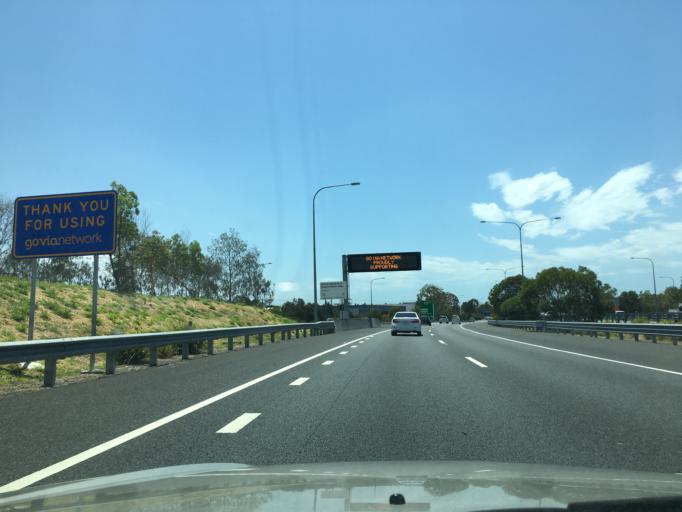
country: AU
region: Queensland
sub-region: Brisbane
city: Wavell Heights
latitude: -27.3922
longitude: 153.0931
